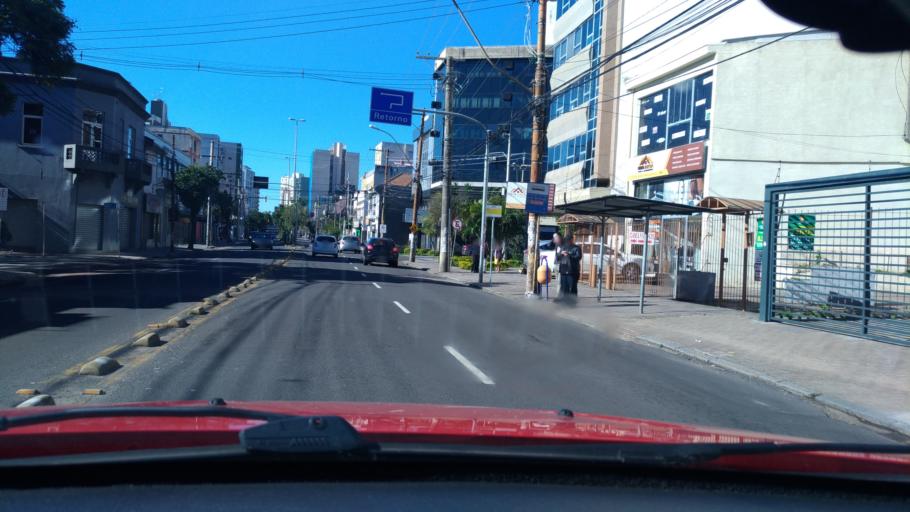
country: BR
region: Rio Grande do Sul
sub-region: Porto Alegre
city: Porto Alegre
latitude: -30.0225
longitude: -51.2090
